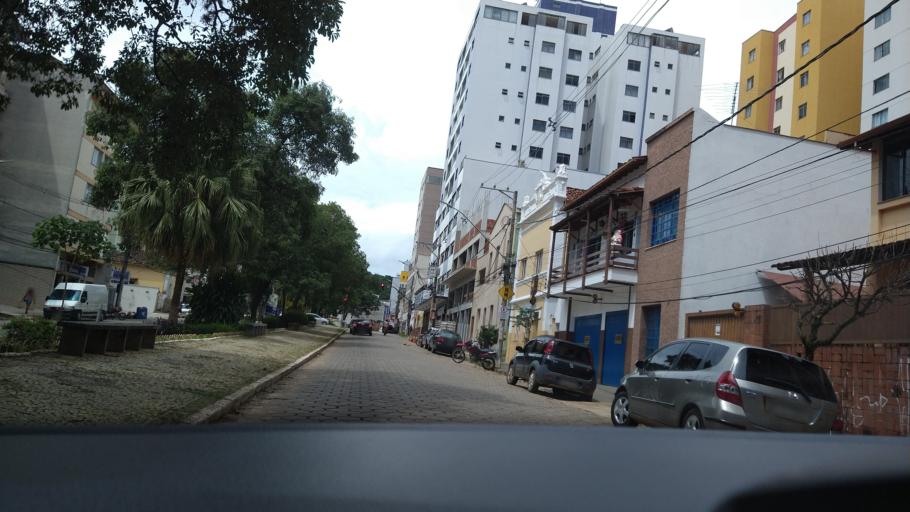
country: BR
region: Minas Gerais
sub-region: Vicosa
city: Vicosa
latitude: -20.7578
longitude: -42.8787
